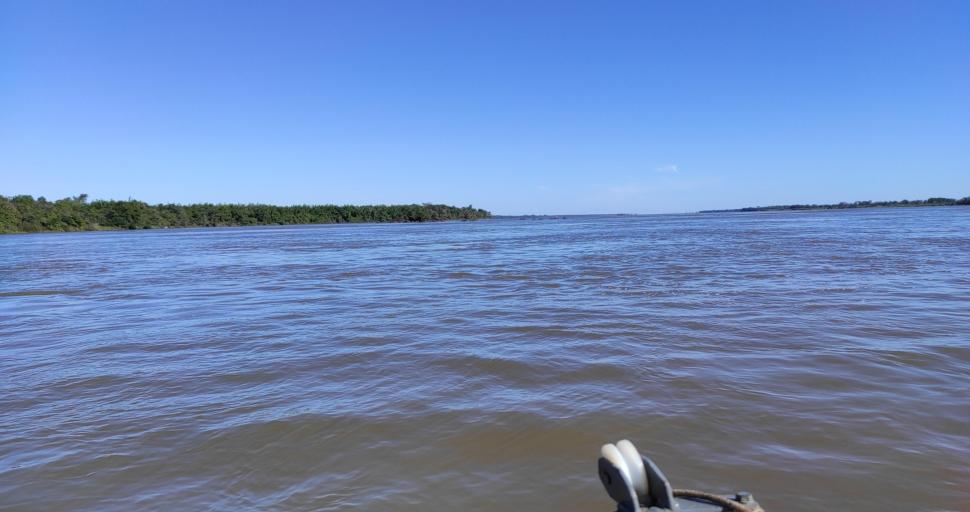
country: AR
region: Corrientes
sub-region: Departamento de Itati
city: Itati
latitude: -27.2774
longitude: -58.3176
